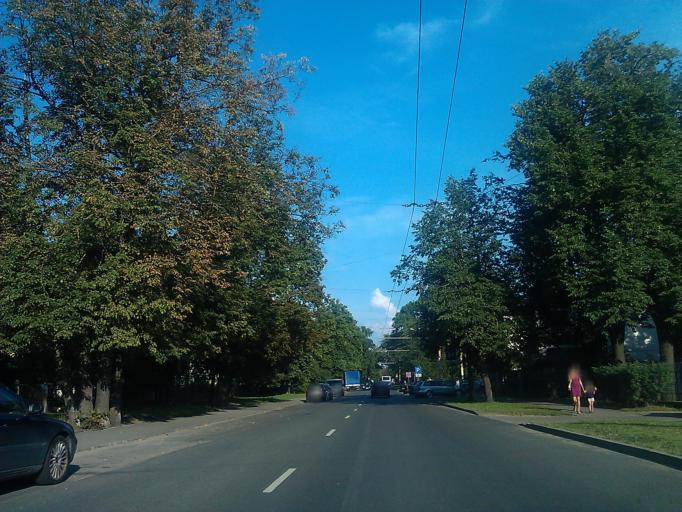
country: LV
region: Riga
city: Jaunciems
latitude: 56.9717
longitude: 24.1710
